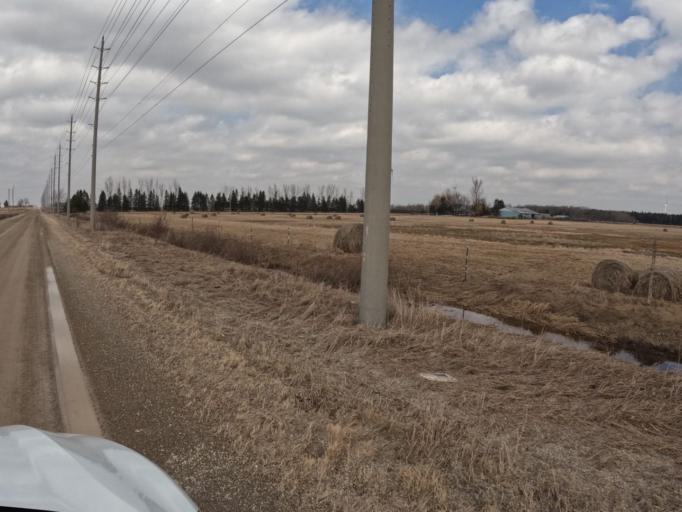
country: CA
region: Ontario
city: Shelburne
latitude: 44.0345
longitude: -80.3161
